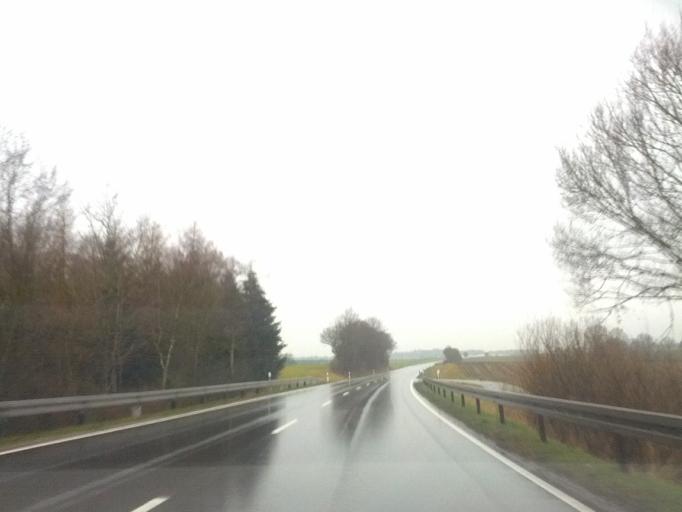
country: DE
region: Baden-Wuerttemberg
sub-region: Tuebingen Region
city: Ochsenhausen
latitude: 48.0695
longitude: 9.9343
